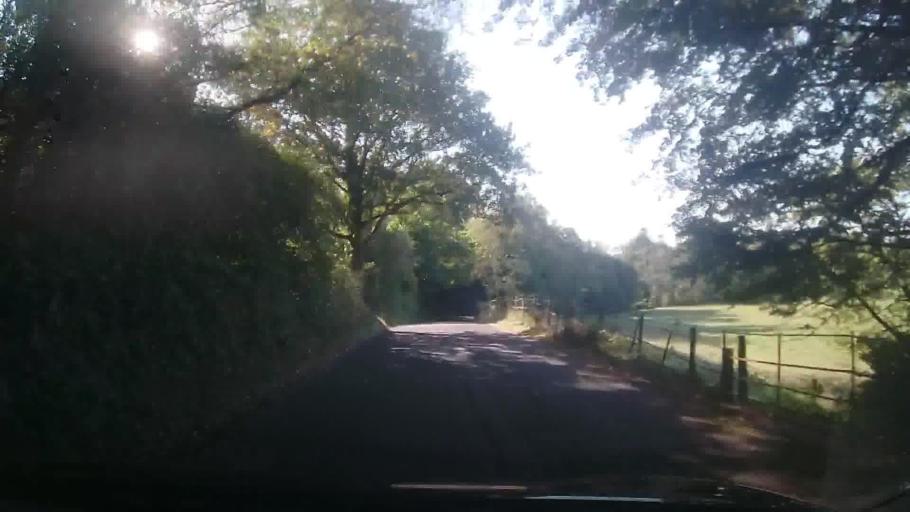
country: GB
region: England
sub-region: Cumbria
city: Seascale
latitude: 54.3957
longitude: -3.3790
